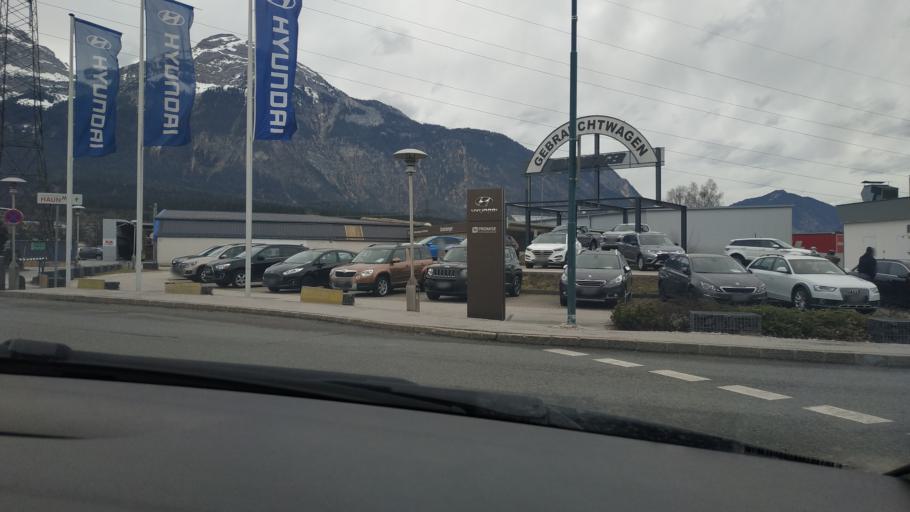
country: AT
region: Tyrol
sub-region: Politischer Bezirk Schwaz
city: Strass im Zillertal
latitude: 47.3977
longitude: 11.8178
